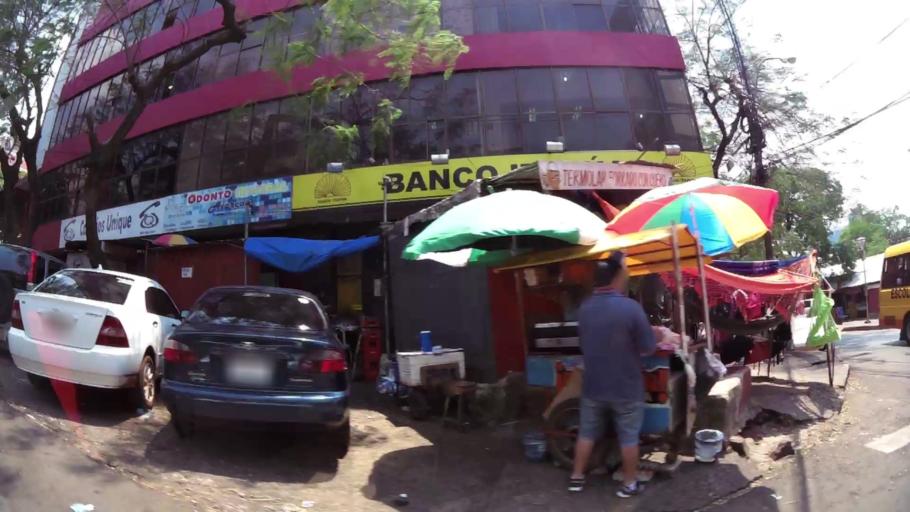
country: PY
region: Alto Parana
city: Ciudad del Este
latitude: -25.5125
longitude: -54.6105
